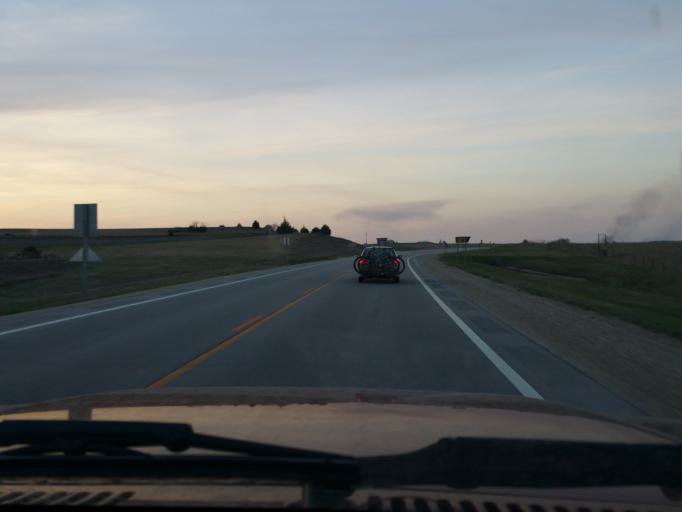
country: US
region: Kansas
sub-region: Riley County
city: Ogden
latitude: 39.2949
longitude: -96.7549
